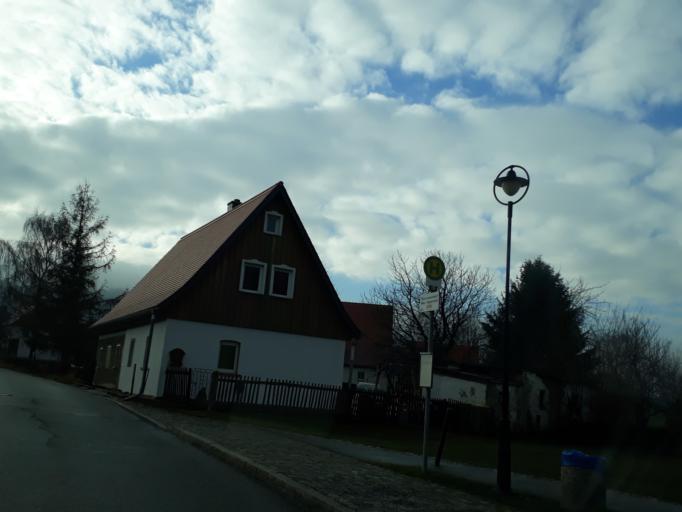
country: DE
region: Saxony
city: Niedercunnersdorf
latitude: 51.0229
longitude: 14.6765
